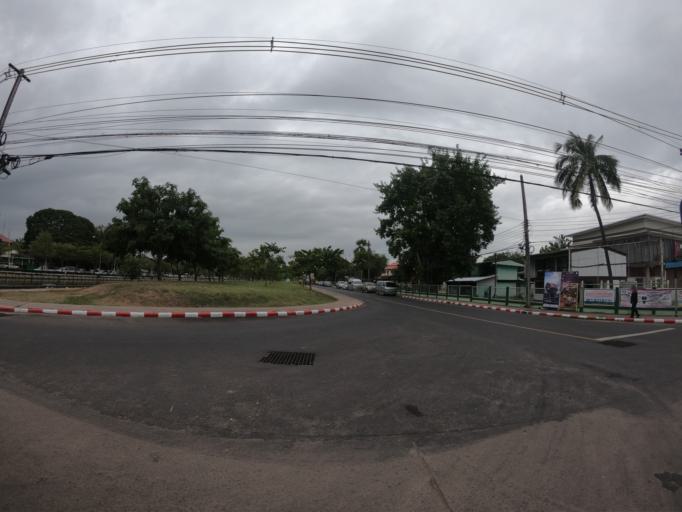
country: TH
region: Roi Et
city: Roi Et
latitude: 16.0501
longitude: 103.6513
